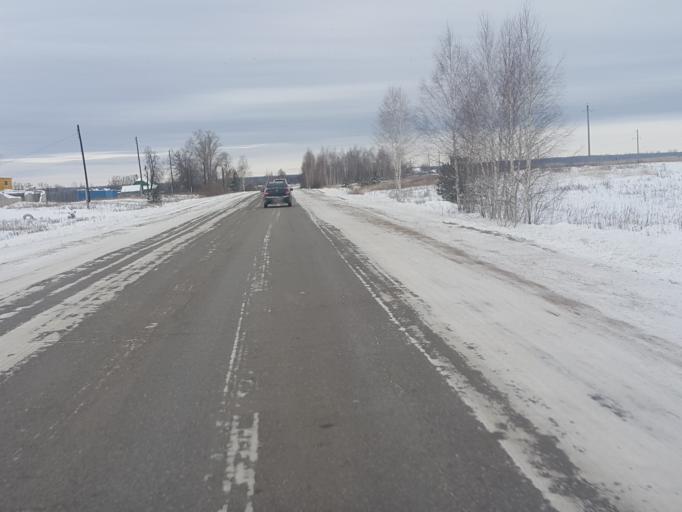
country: RU
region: Tambov
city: Platonovka
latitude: 52.8590
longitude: 41.8364
